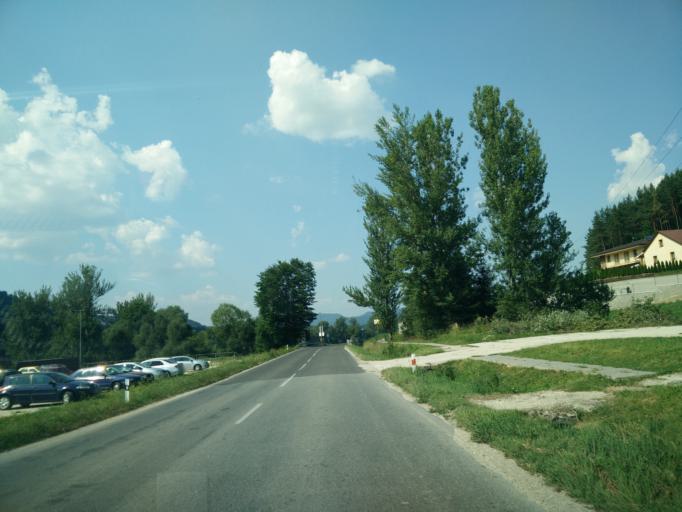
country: SK
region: Zilinsky
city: Rajec
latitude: 49.0458
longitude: 18.6214
